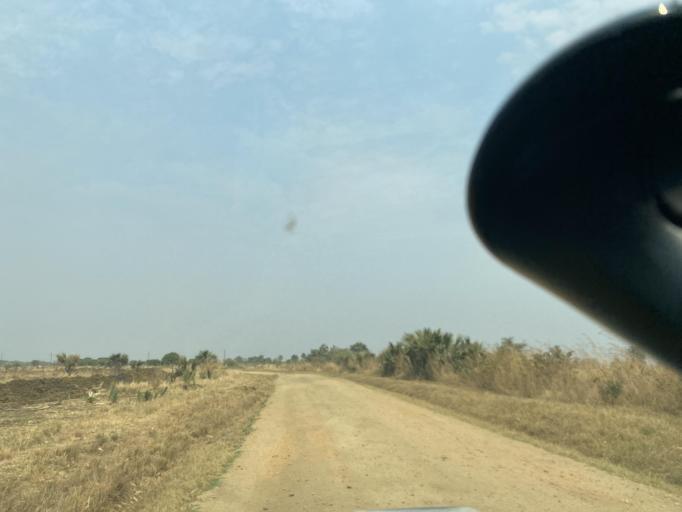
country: ZM
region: Lusaka
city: Kafue
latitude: -15.6508
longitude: 28.0584
